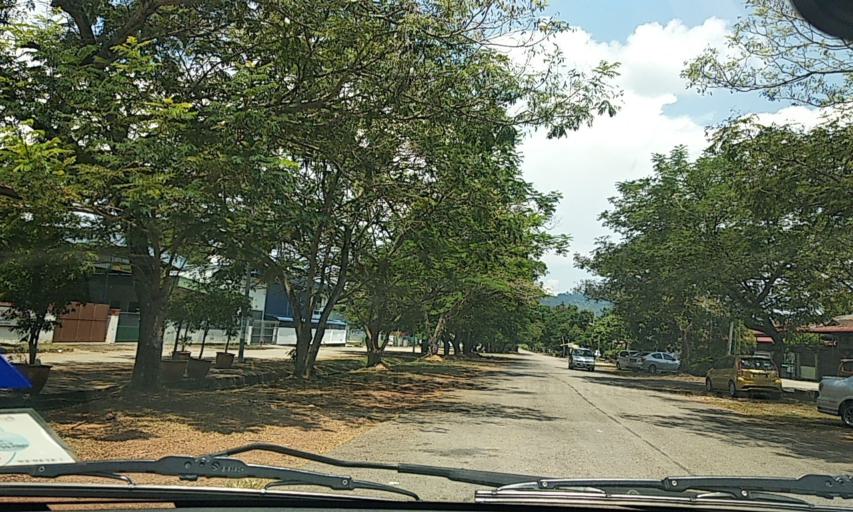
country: MY
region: Kedah
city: Sungai Petani
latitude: 5.6241
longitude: 100.4724
